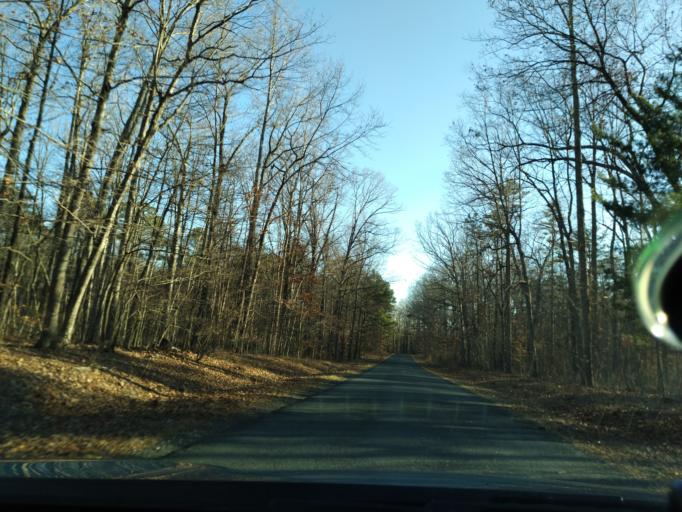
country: US
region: Virginia
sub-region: Appomattox County
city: Appomattox
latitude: 37.3927
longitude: -78.6582
